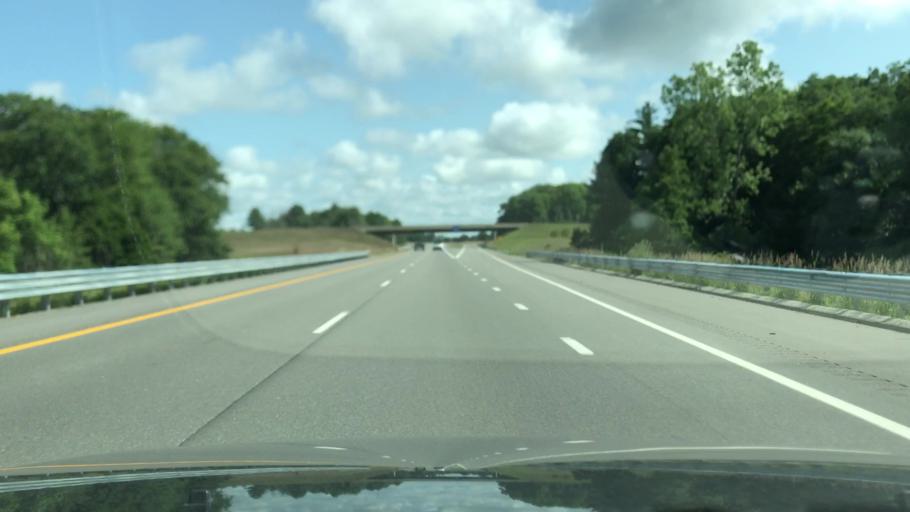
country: US
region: Michigan
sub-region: Montcalm County
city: Howard City
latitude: 43.4549
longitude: -85.4816
